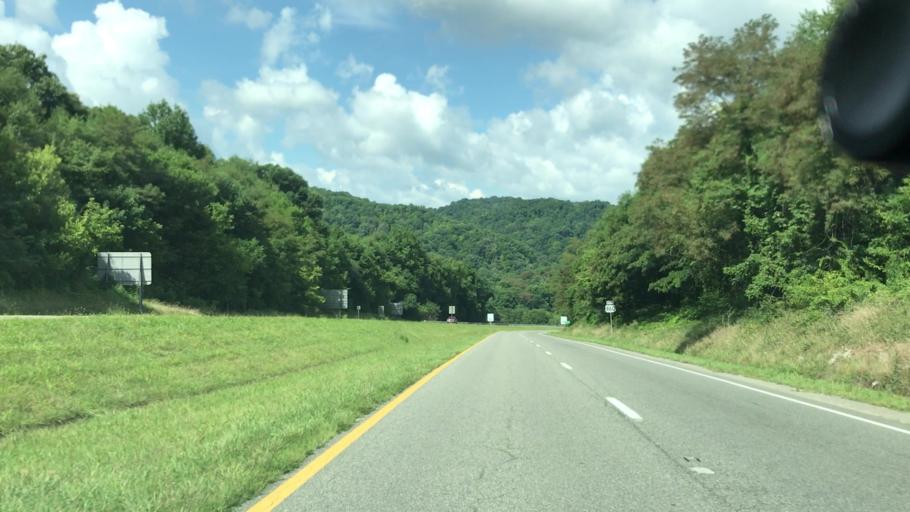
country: US
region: Virginia
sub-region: Giles County
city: Pearisburg
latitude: 37.3352
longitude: -80.7447
